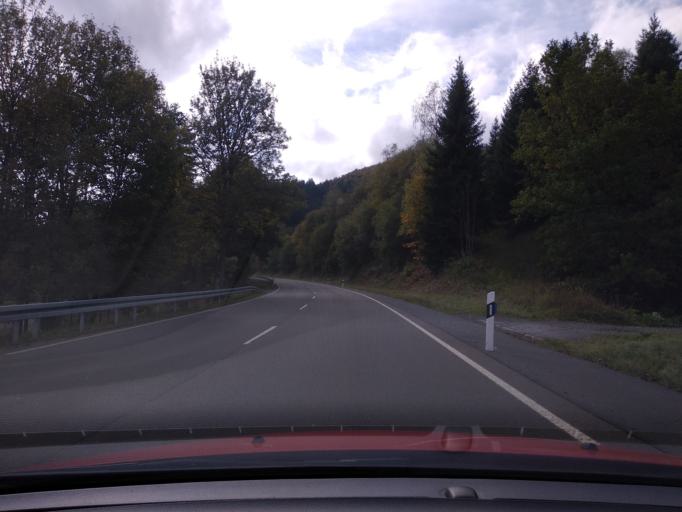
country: DE
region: North Rhine-Westphalia
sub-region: Regierungsbezirk Arnsberg
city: Bestwig
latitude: 51.2888
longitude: 8.3946
